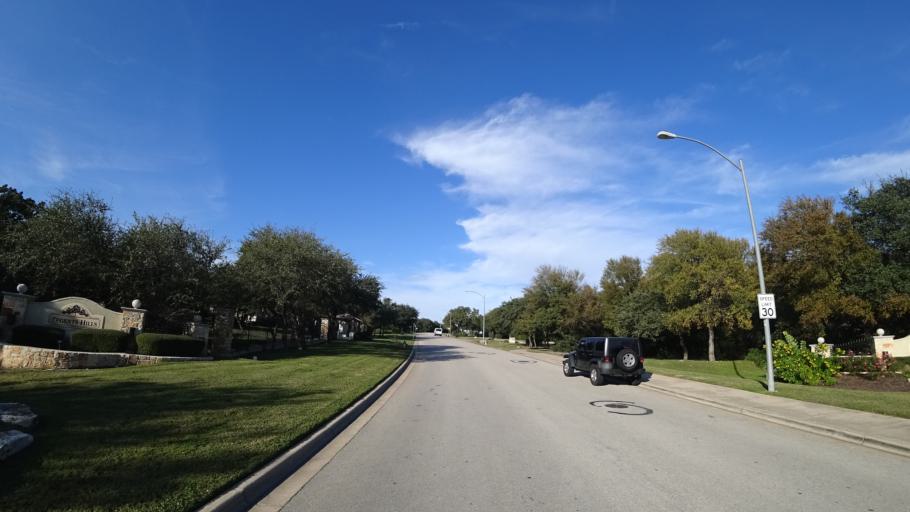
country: US
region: Texas
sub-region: Travis County
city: Barton Creek
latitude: 30.2563
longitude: -97.8444
